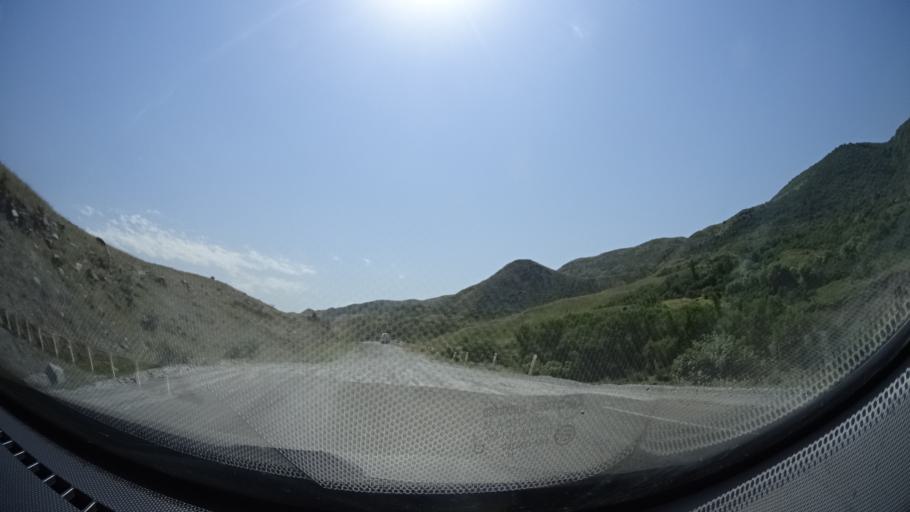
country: GE
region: Samtskhe-Javakheti
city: Aspindza
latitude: 41.5927
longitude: 43.1725
